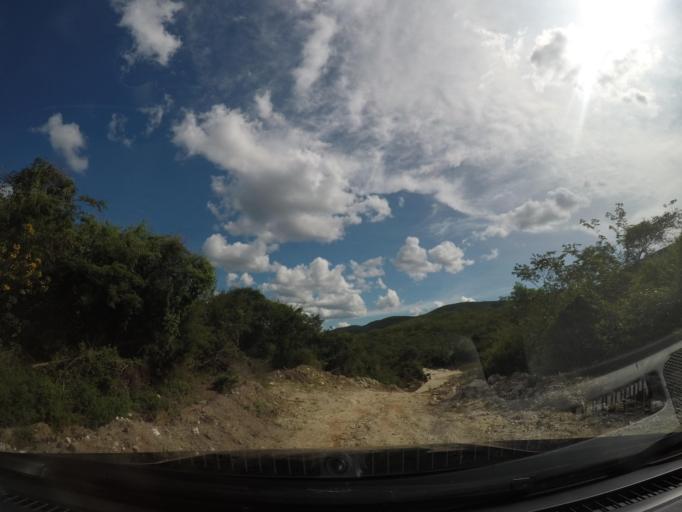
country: BR
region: Bahia
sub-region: Barra Da Estiva
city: Barra da Estiva
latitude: -13.1404
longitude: -41.5954
